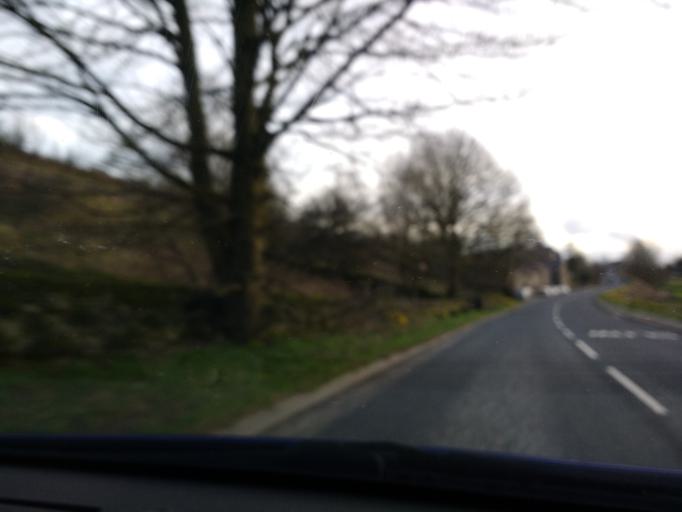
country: GB
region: England
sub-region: North Yorkshire
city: Settle
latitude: 54.0887
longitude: -2.2731
